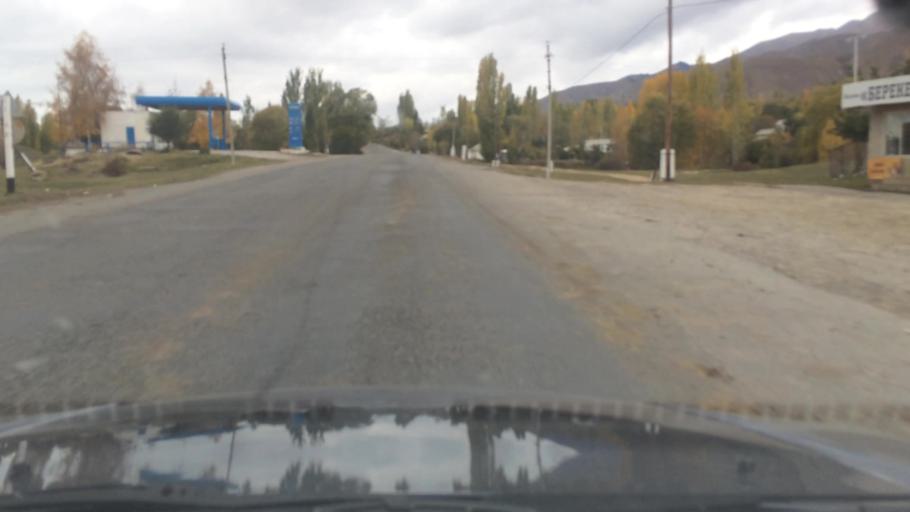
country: KG
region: Ysyk-Koel
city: Tyup
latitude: 42.7485
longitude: 78.1192
